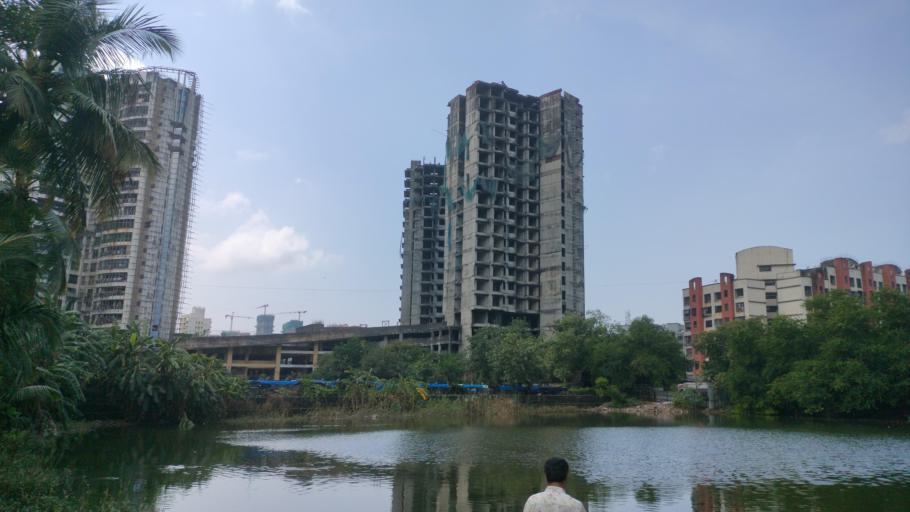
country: IN
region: Maharashtra
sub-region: Mumbai Suburban
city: Borivli
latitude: 19.2105
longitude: 72.8324
